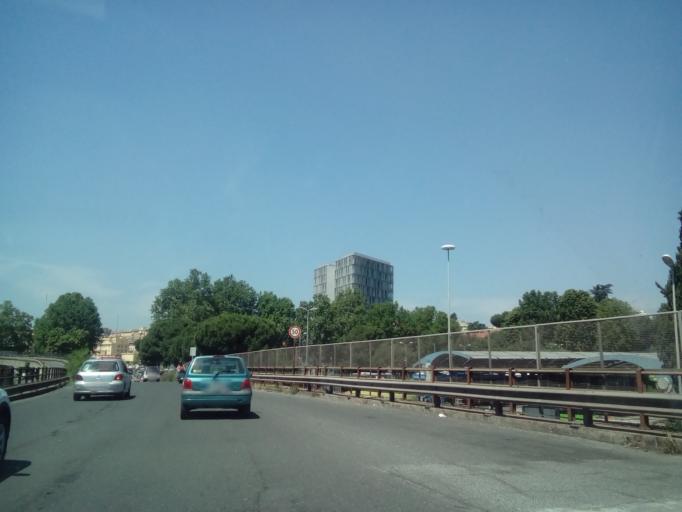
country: IT
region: Latium
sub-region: Citta metropolitana di Roma Capitale
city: Rome
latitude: 41.9087
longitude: 12.5292
